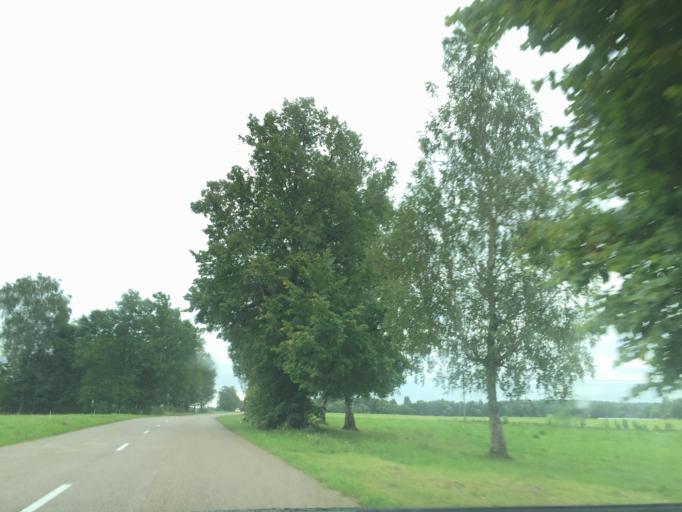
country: LV
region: Varkava
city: Vecvarkava
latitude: 56.4157
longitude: 26.4636
